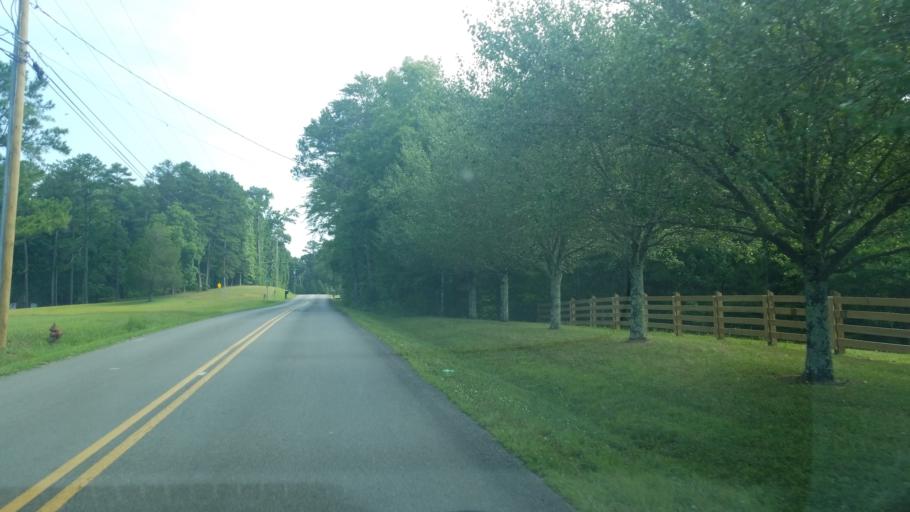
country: US
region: Tennessee
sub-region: Hamilton County
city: Apison
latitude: 35.0450
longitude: -84.9902
